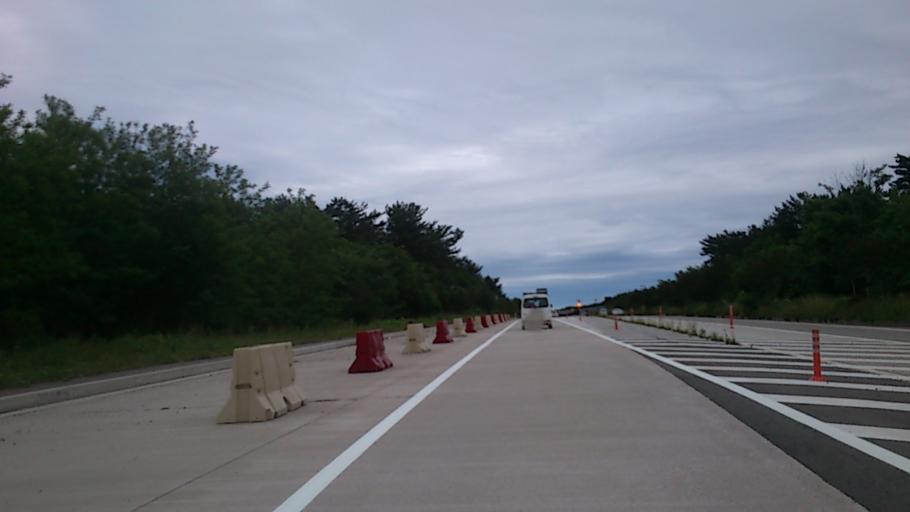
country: JP
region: Akita
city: Akita Shi
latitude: 39.7073
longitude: 140.0722
